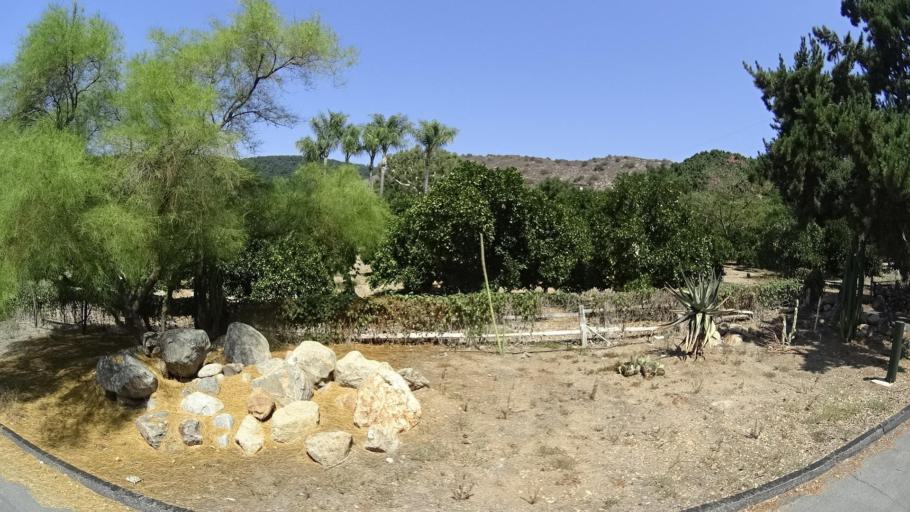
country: US
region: California
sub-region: San Diego County
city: Valley Center
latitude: 33.2920
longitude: -116.9578
